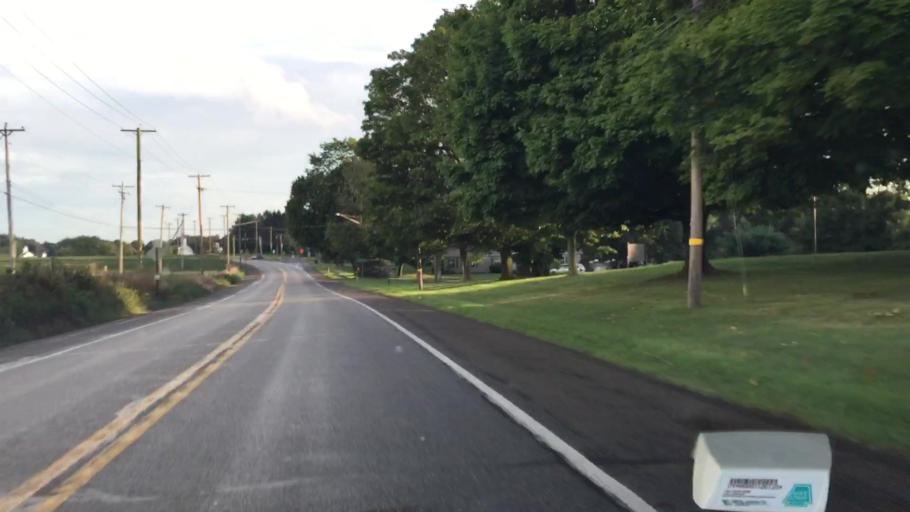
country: US
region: Pennsylvania
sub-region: Butler County
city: Meridian
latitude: 40.8251
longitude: -80.0111
